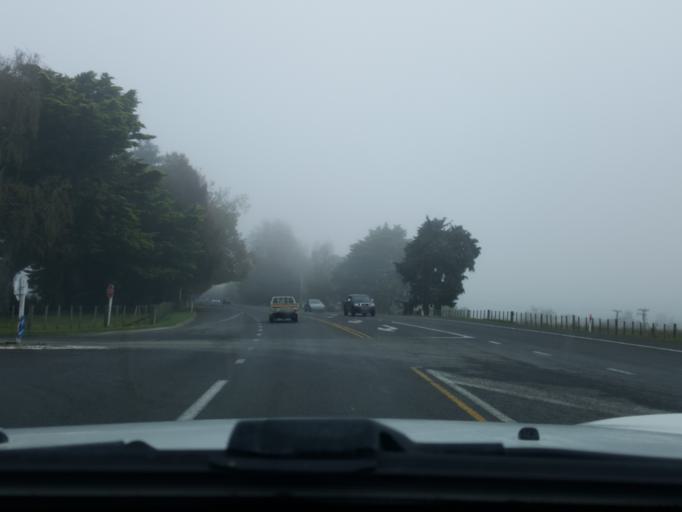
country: NZ
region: Waikato
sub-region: Waikato District
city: Ngaruawahia
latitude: -37.6962
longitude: 175.1931
